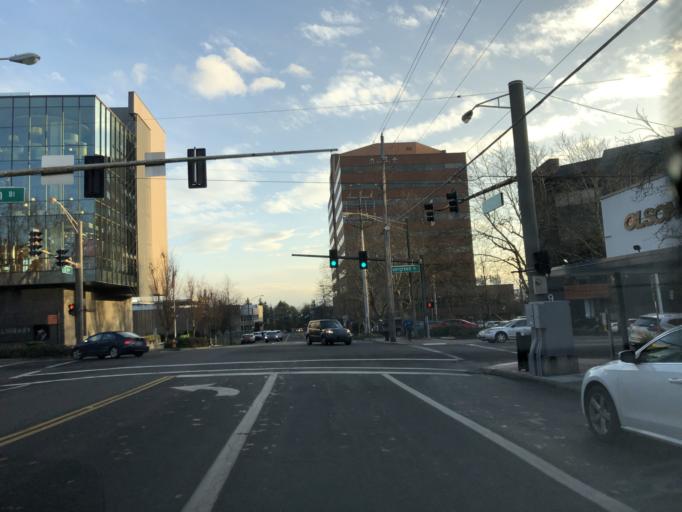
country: US
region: Washington
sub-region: Clark County
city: Vancouver
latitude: 45.6290
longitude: -122.6695
